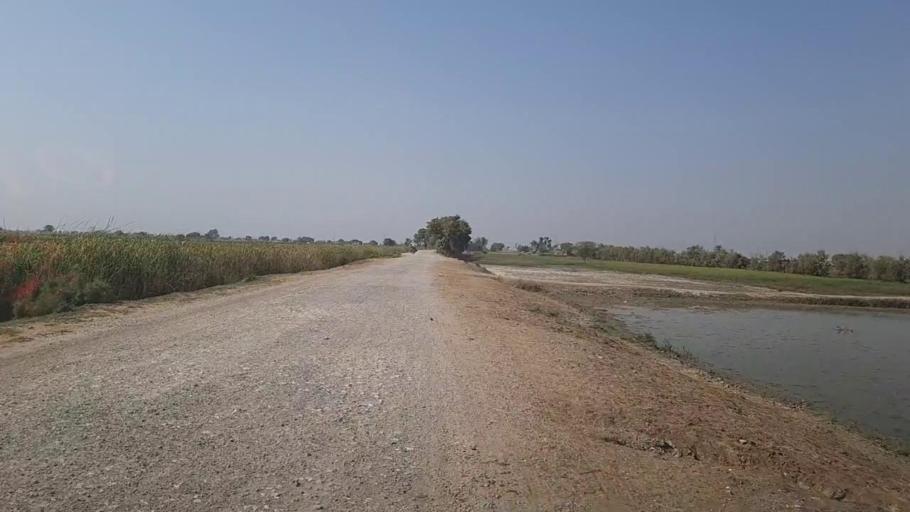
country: PK
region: Sindh
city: Kandhkot
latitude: 28.4023
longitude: 69.2606
